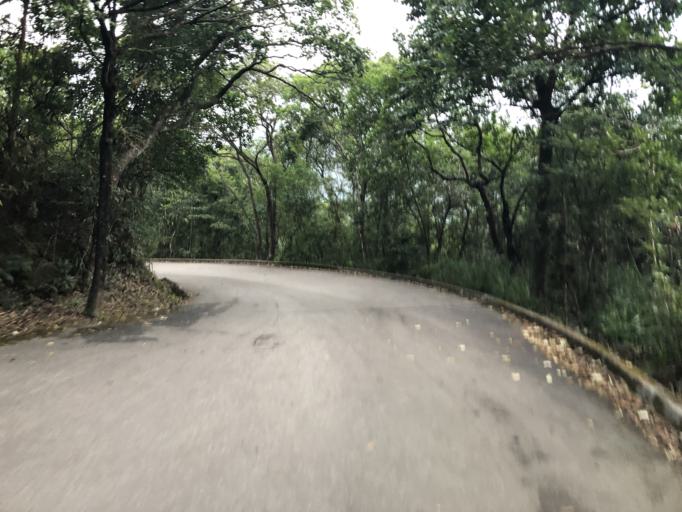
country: HK
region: Wanchai
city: Wan Chai
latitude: 22.2647
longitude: 114.2147
